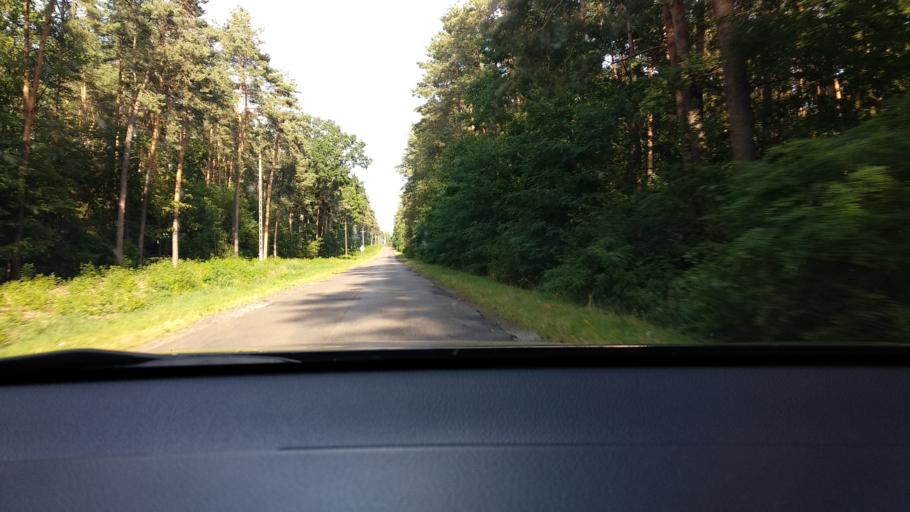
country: PL
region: Masovian Voivodeship
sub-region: Powiat pultuski
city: Pultusk
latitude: 52.7129
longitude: 21.1610
